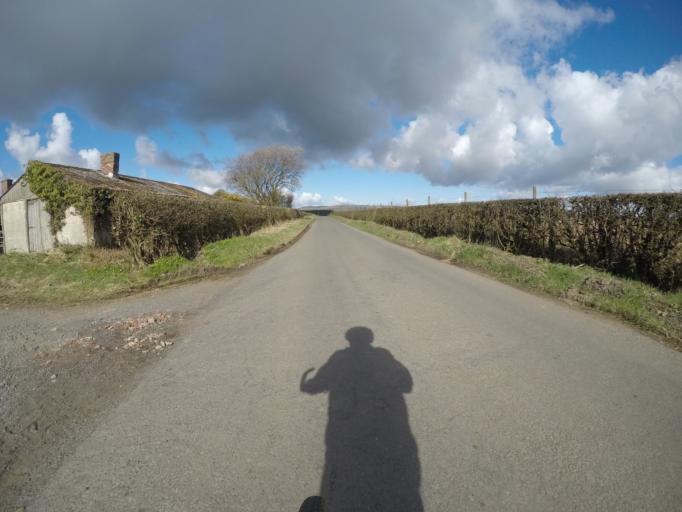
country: GB
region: Scotland
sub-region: North Ayrshire
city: Kilwinning
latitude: 55.6883
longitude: -4.6642
